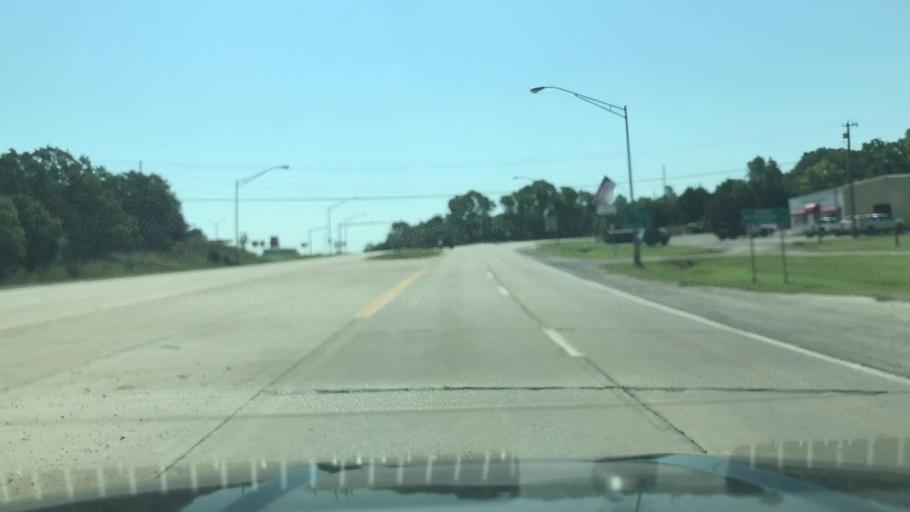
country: US
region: Oklahoma
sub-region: Creek County
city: Drumright
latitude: 35.9880
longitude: -96.5860
